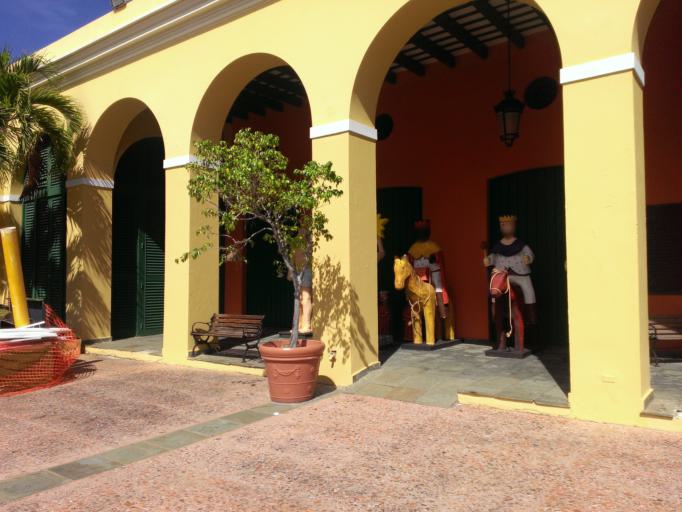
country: PR
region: San Juan
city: San Juan
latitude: 18.4681
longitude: -66.1174
